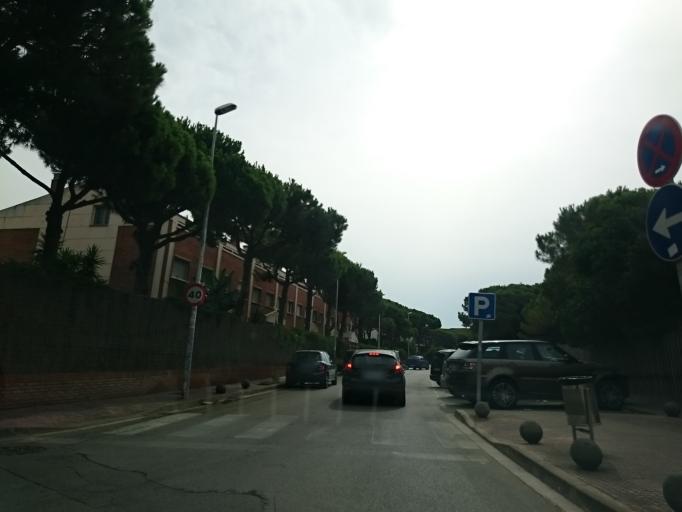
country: ES
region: Catalonia
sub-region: Provincia de Barcelona
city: Gava
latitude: 41.2671
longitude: 2.0093
